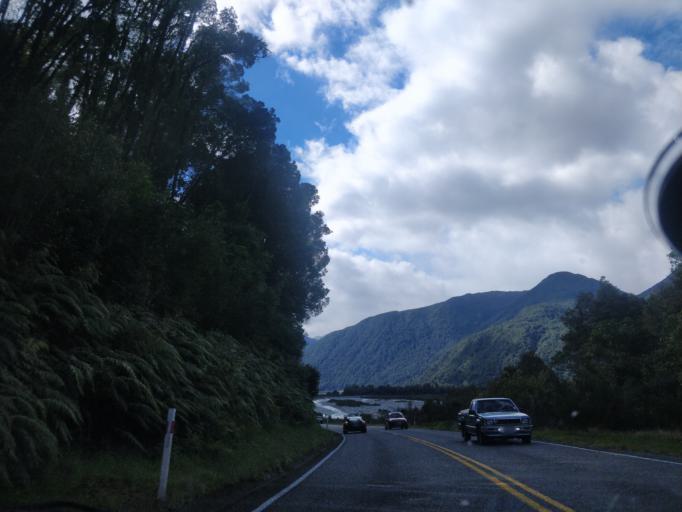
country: NZ
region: West Coast
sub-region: Grey District
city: Greymouth
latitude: -42.7953
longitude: 171.5883
